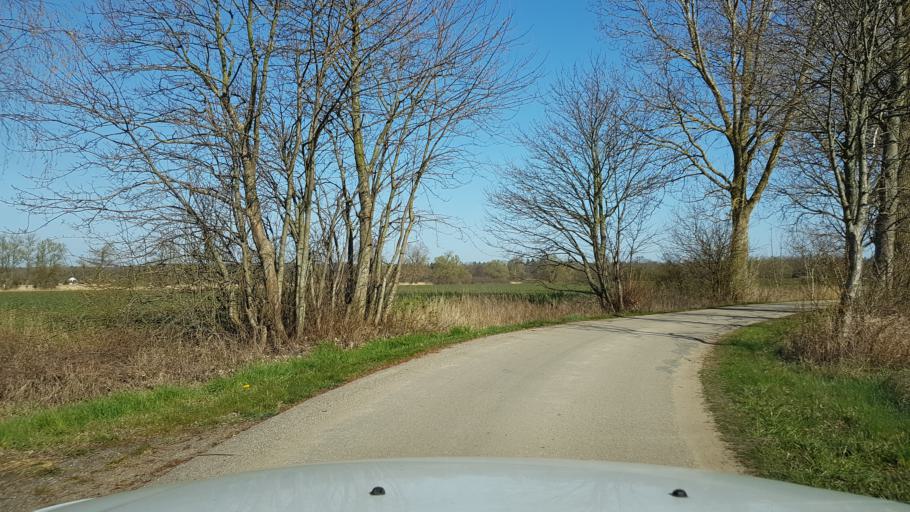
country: PL
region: West Pomeranian Voivodeship
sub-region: Powiat kolobrzeski
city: Ustronie Morskie
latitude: 54.2255
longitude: 15.8340
